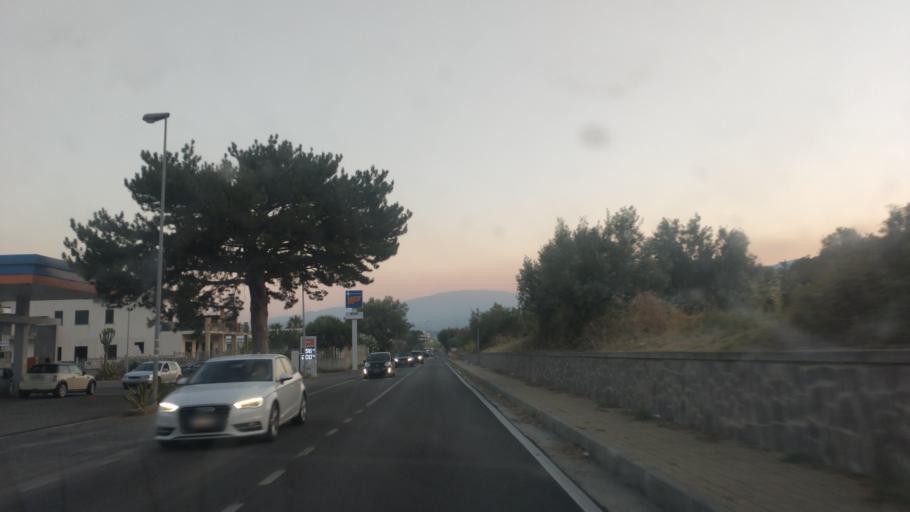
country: IT
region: Calabria
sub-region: Provincia di Catanzaro
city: Montepaone Lido
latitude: 38.7379
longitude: 16.5471
